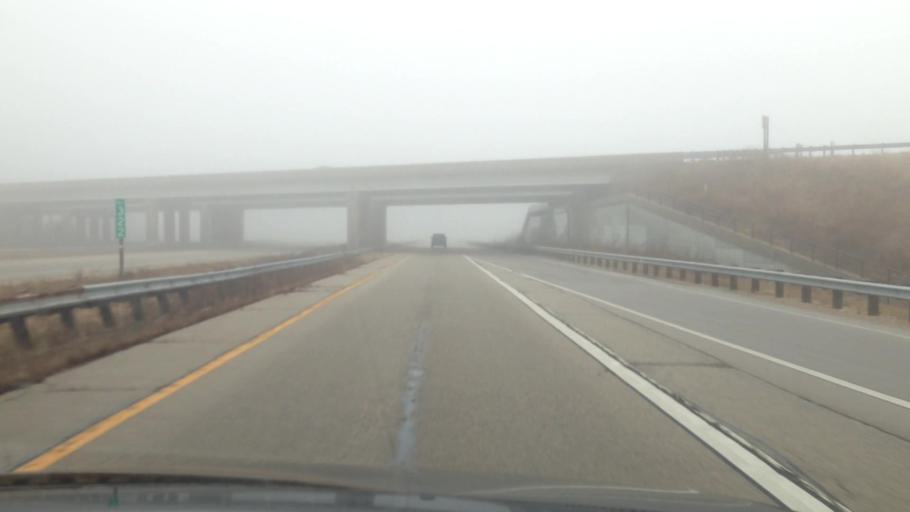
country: US
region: Wisconsin
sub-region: Walworth County
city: Elkhorn
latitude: 42.6690
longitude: -88.5175
